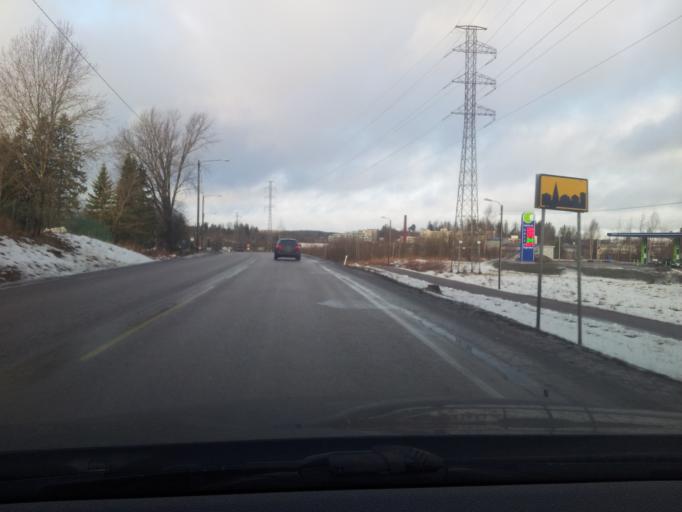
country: FI
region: Uusimaa
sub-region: Helsinki
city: Espoo
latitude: 60.1839
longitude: 24.6023
